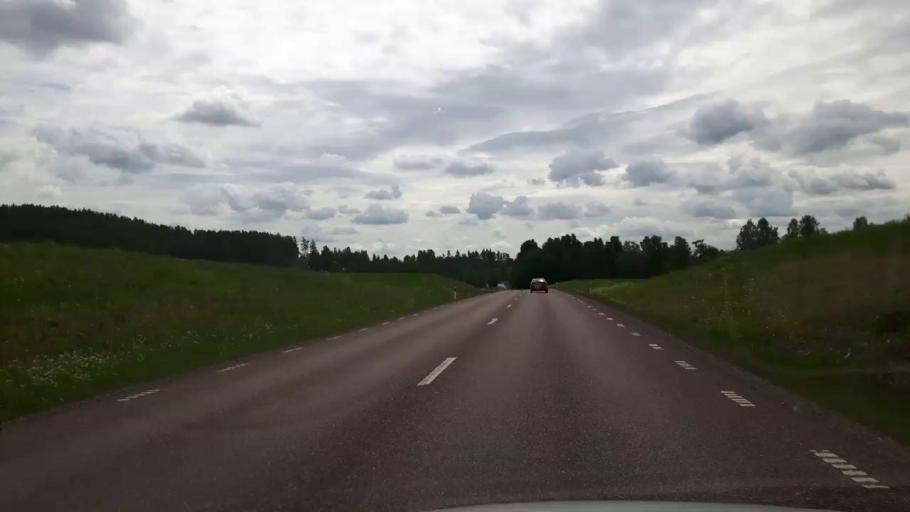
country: SE
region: Dalarna
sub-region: Hedemora Kommun
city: Hedemora
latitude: 60.3281
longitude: 15.9501
